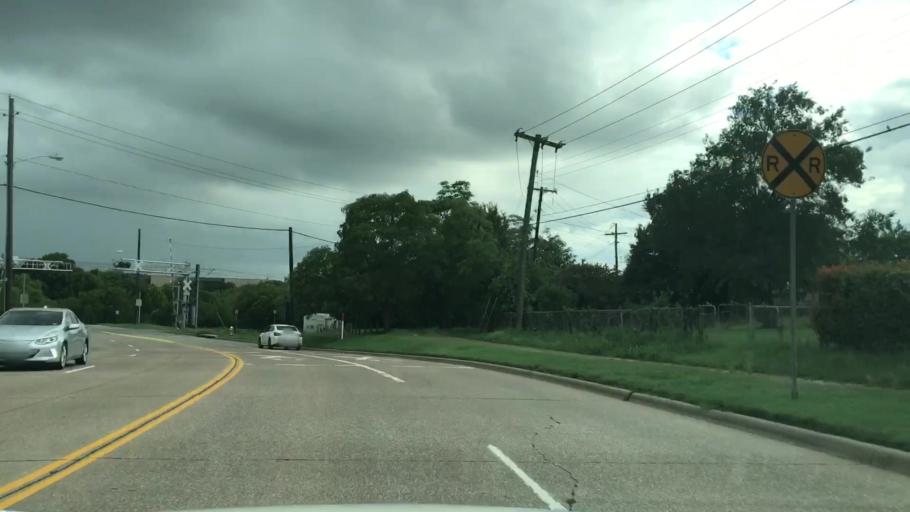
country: US
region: Texas
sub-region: Dallas County
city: Richardson
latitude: 32.9170
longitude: -96.7545
